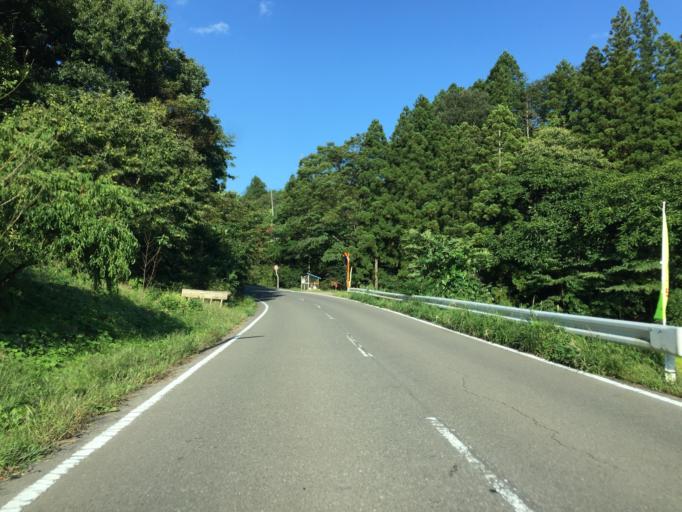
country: JP
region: Fukushima
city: Fukushima-shi
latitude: 37.7218
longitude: 140.5164
